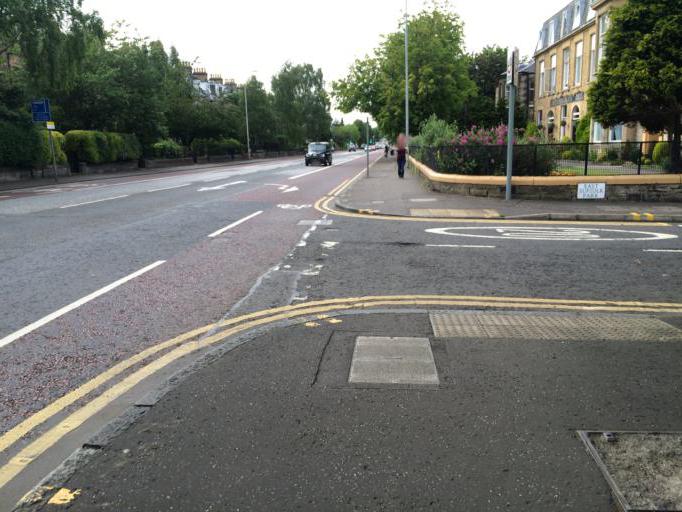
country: GB
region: Scotland
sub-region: Edinburgh
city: Edinburgh
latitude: 55.9276
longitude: -3.1678
